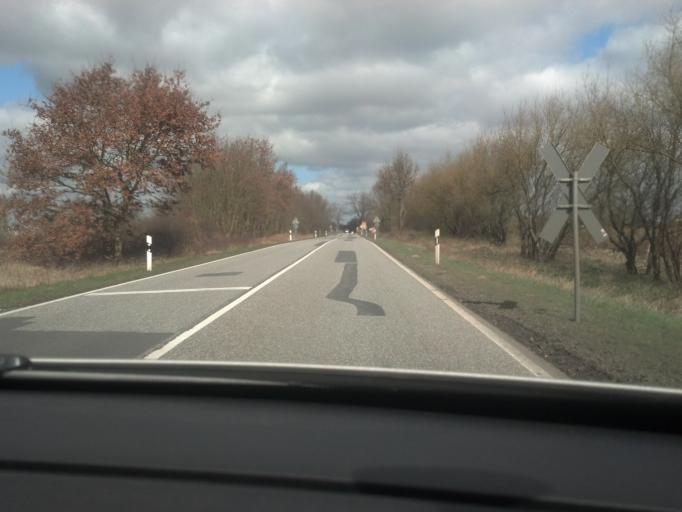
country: DE
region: Mecklenburg-Vorpommern
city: Plau am See
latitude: 53.3769
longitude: 12.2476
